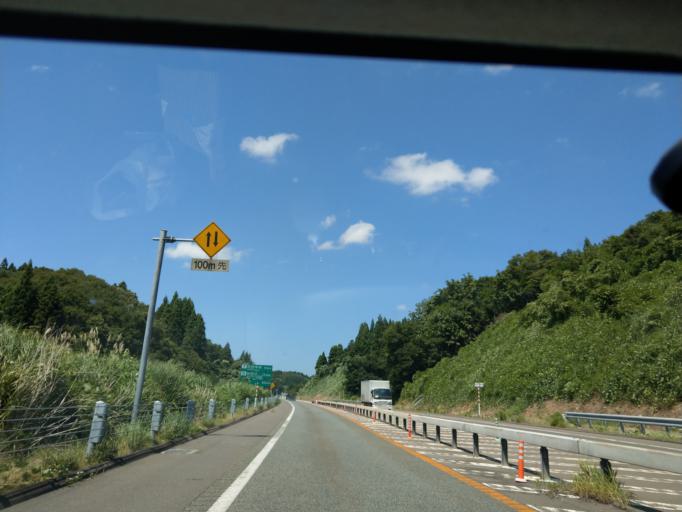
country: JP
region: Akita
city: Akita
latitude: 39.6709
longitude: 140.1880
